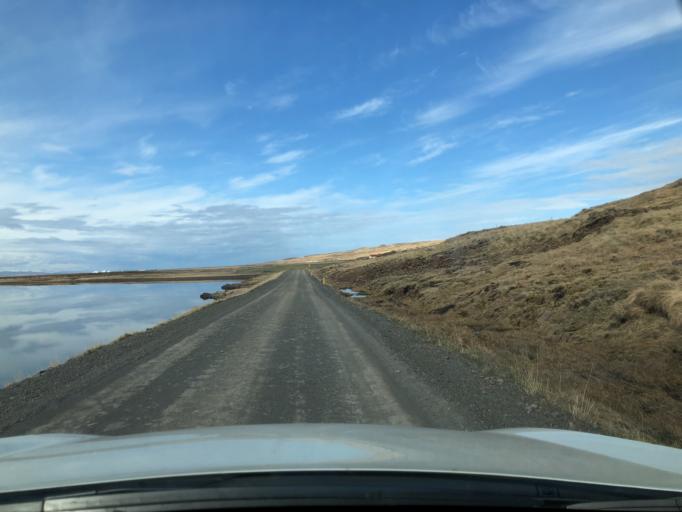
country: IS
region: West
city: Borgarnes
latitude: 65.0561
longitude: -21.6498
